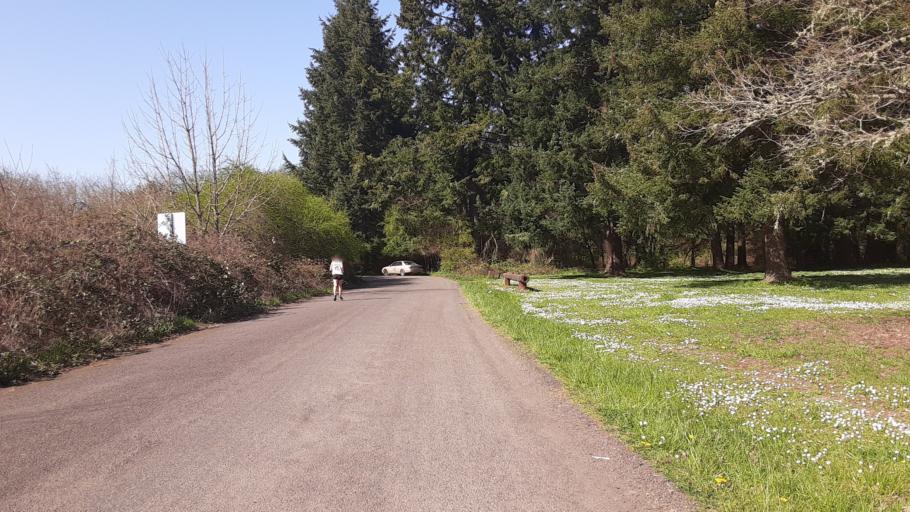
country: US
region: Oregon
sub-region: Benton County
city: Corvallis
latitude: 44.5381
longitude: -123.2537
